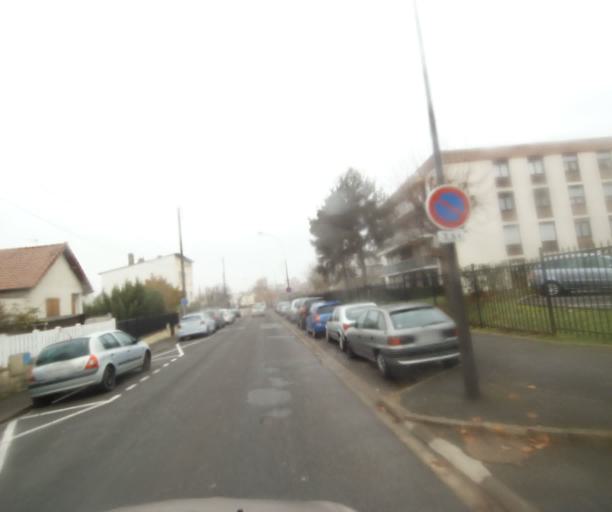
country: FR
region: Ile-de-France
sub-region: Departement de Seine-Saint-Denis
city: Vaujours
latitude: 48.9361
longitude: 2.5725
